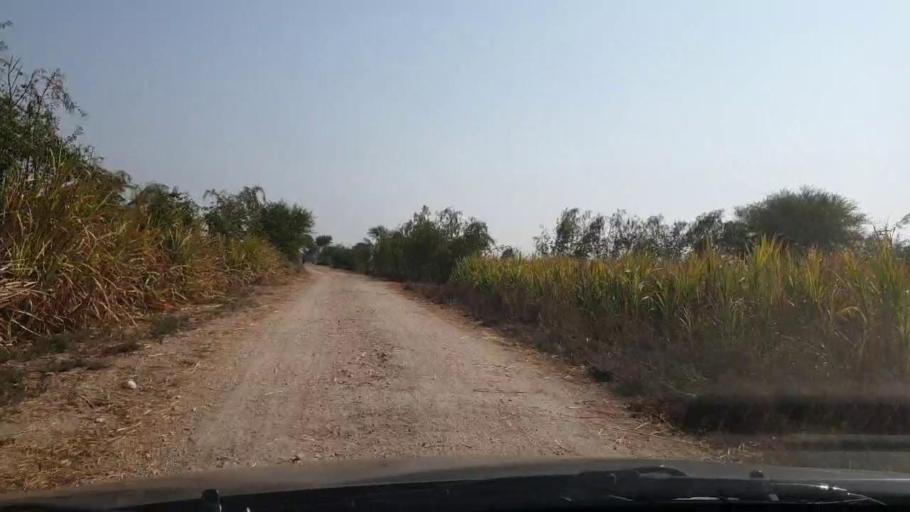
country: PK
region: Sindh
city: Jhol
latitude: 25.8596
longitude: 69.0020
